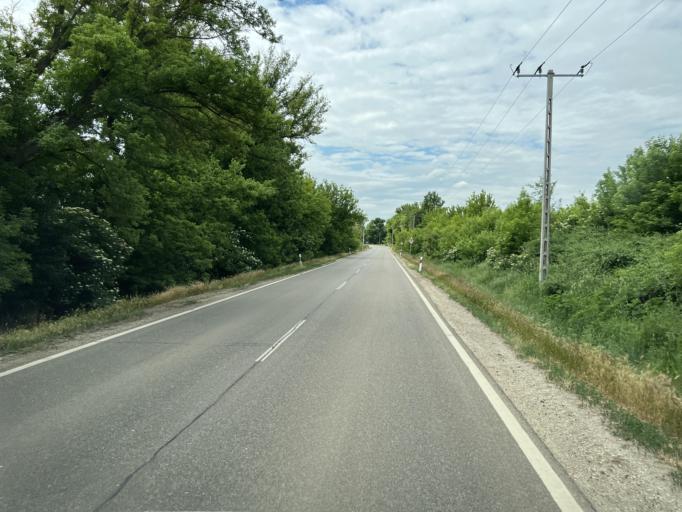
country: HU
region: Pest
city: Koka
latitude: 47.4982
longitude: 19.5856
